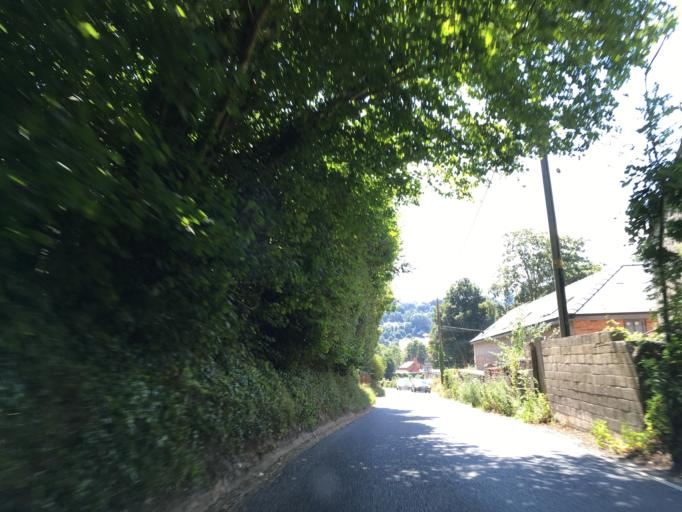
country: GB
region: England
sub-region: Gloucestershire
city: Brimscombe
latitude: 51.7217
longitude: -2.1798
